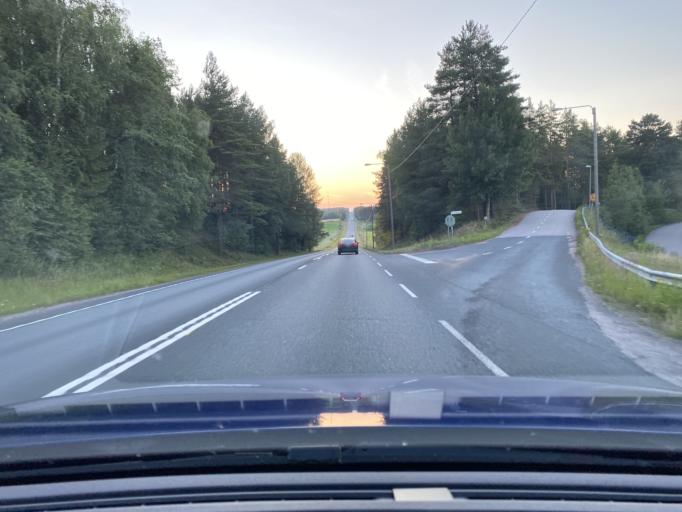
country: FI
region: Pirkanmaa
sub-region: Luoteis-Pirkanmaa
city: Ikaalinen
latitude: 61.7648
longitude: 23.0204
